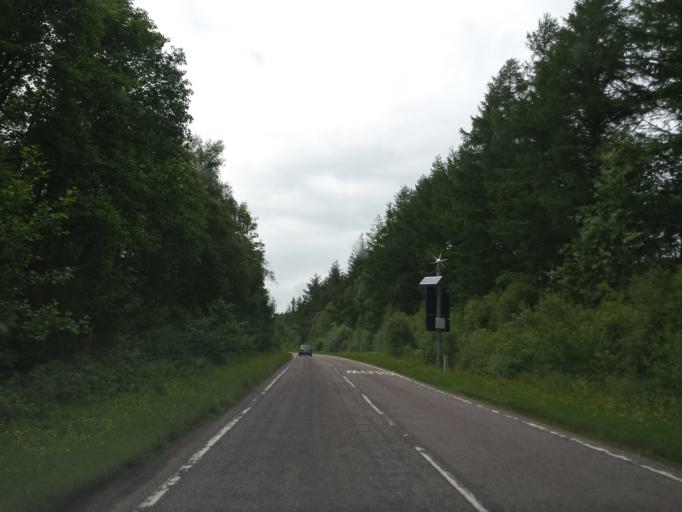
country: GB
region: Scotland
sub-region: Highland
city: Fort William
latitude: 56.8556
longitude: -5.1948
